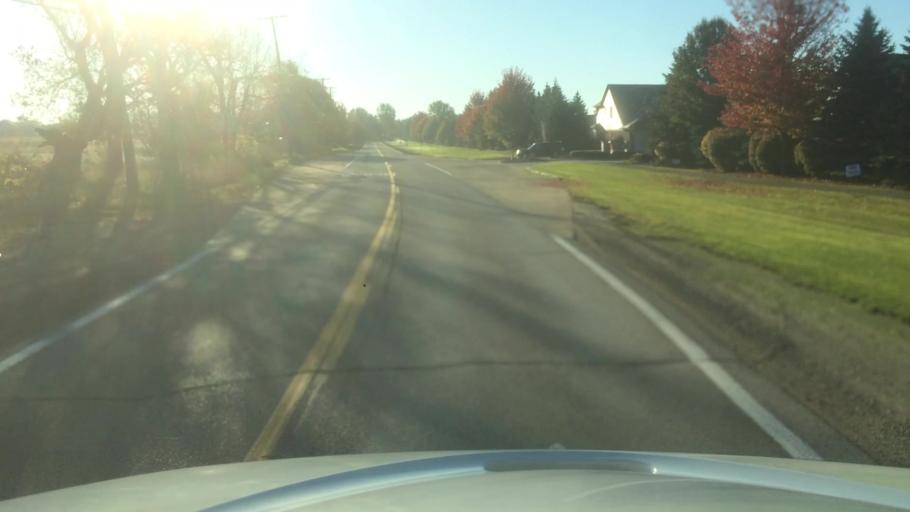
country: US
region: Michigan
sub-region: Macomb County
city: Shelby
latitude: 42.6844
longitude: -82.9511
